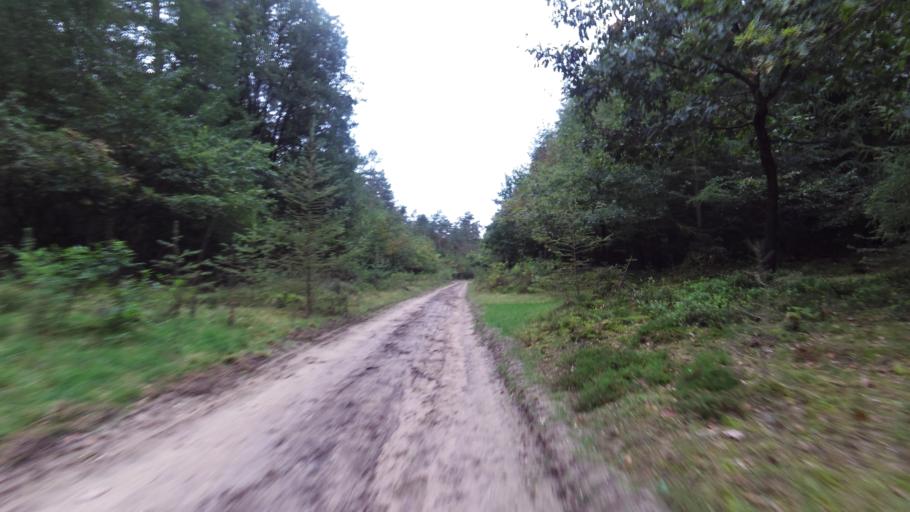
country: NL
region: Gelderland
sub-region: Gemeente Apeldoorn
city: Beekbergen
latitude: 52.1546
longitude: 5.8970
